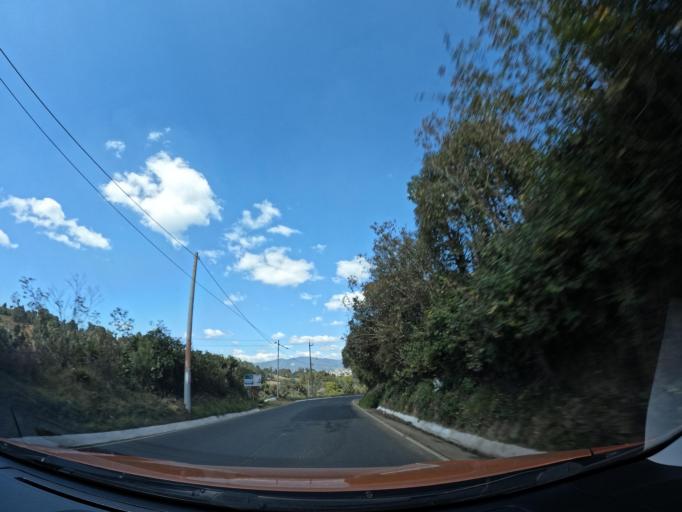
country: GT
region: Chimaltenango
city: Patzun
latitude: 14.6588
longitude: -91.0195
